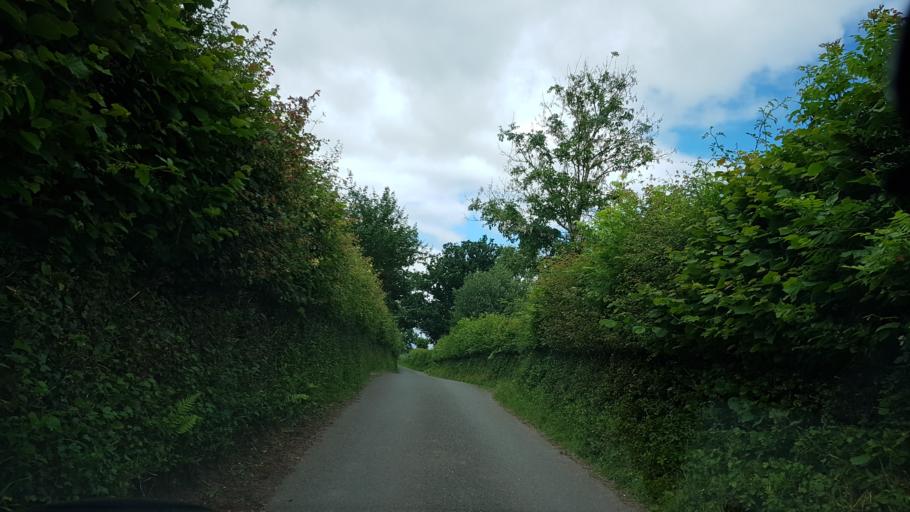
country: GB
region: Wales
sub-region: Monmouthshire
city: Llanarth
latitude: 51.8210
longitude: -2.8617
